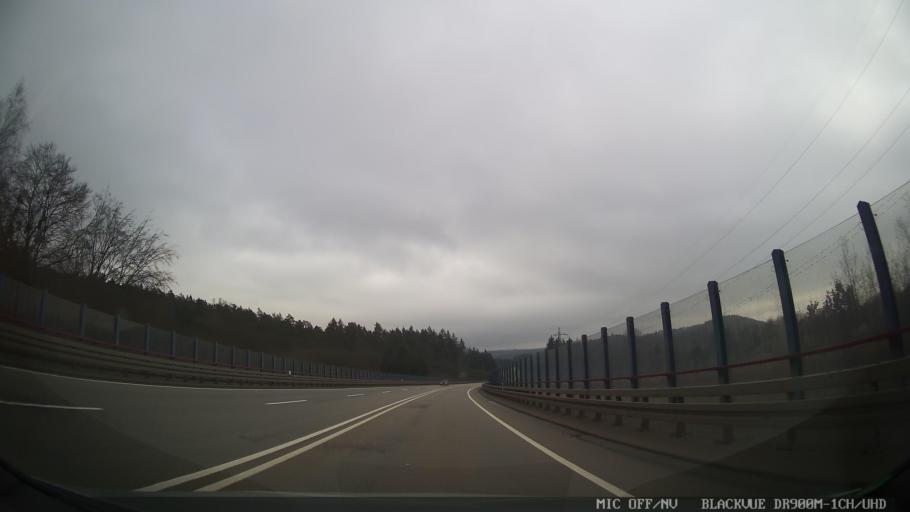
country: DE
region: Saarland
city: Mettlach
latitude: 49.4784
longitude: 6.6251
